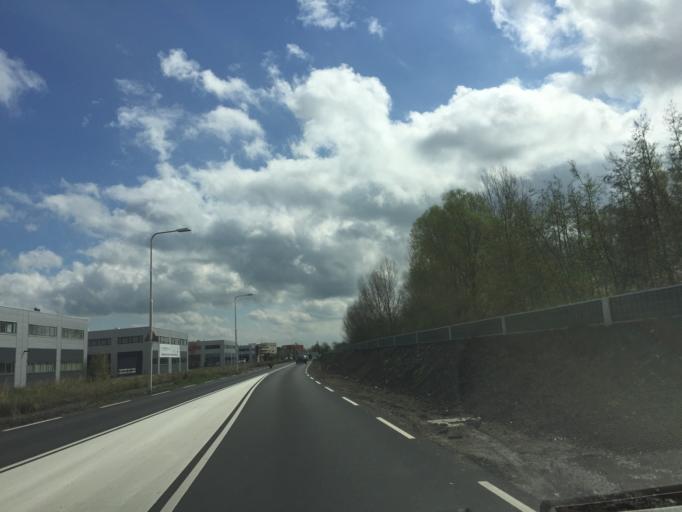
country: NL
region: South Holland
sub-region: Bodegraven-Reeuwijk
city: Reeuwijk
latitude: 52.0392
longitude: 4.7123
